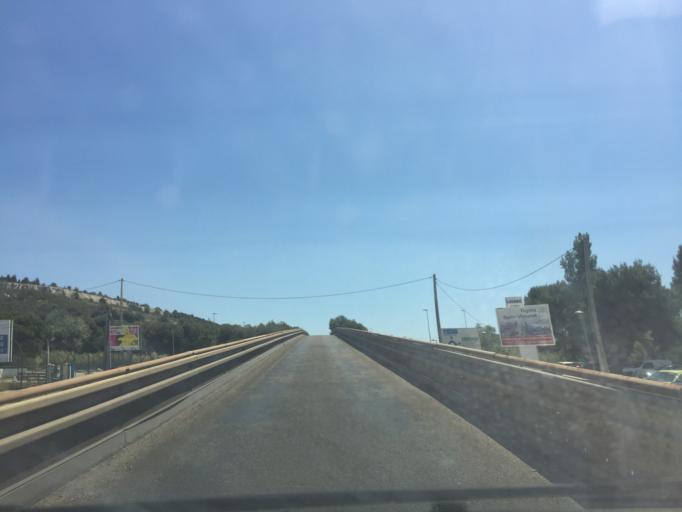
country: FR
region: Provence-Alpes-Cote d'Azur
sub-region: Departement des Bouches-du-Rhone
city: Vitrolles
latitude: 43.4607
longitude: 5.2326
